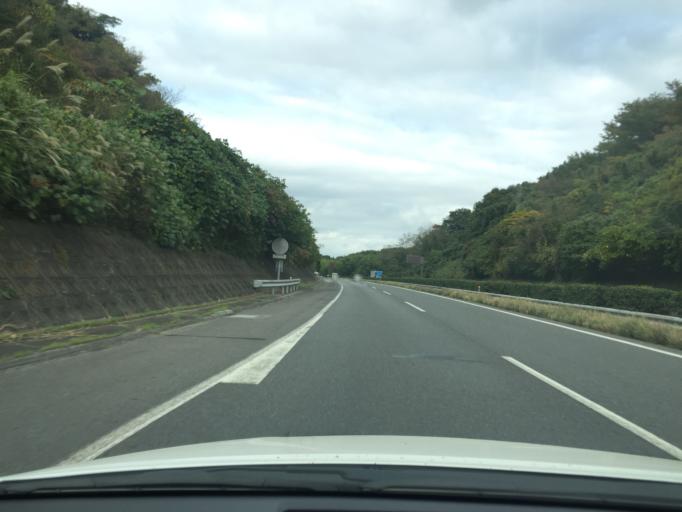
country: JP
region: Fukushima
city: Iwaki
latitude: 37.0062
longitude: 140.8123
